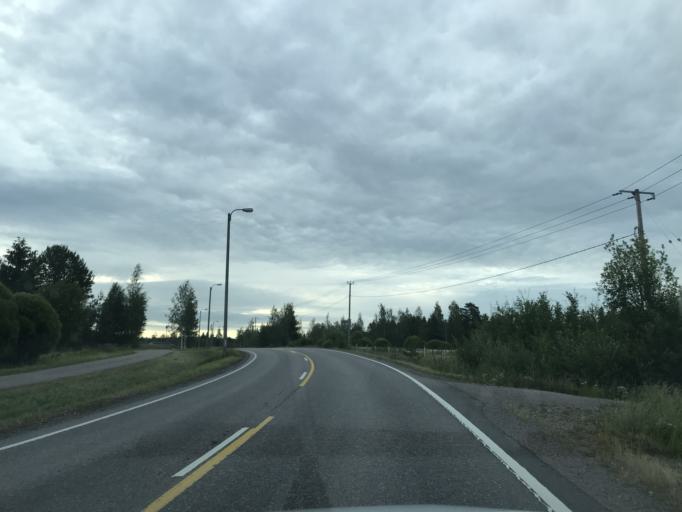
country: FI
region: Uusimaa
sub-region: Helsinki
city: Nurmijaervi
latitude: 60.3847
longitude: 24.7158
